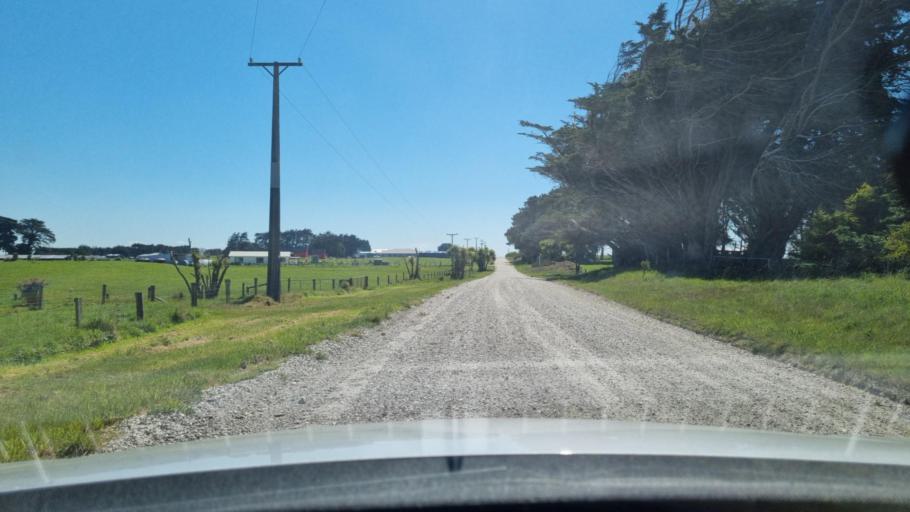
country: NZ
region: Southland
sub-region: Invercargill City
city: Invercargill
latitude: -46.4150
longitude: 168.2634
